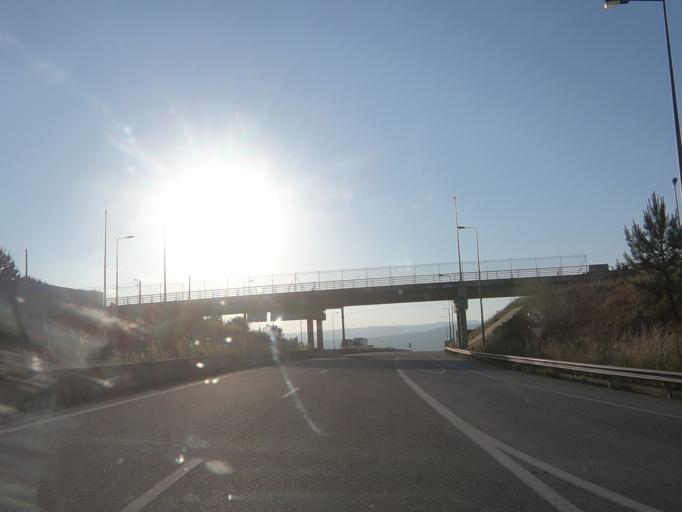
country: PT
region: Guarda
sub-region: Celorico da Beira
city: Celorico da Beira
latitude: 40.6247
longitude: -7.4011
